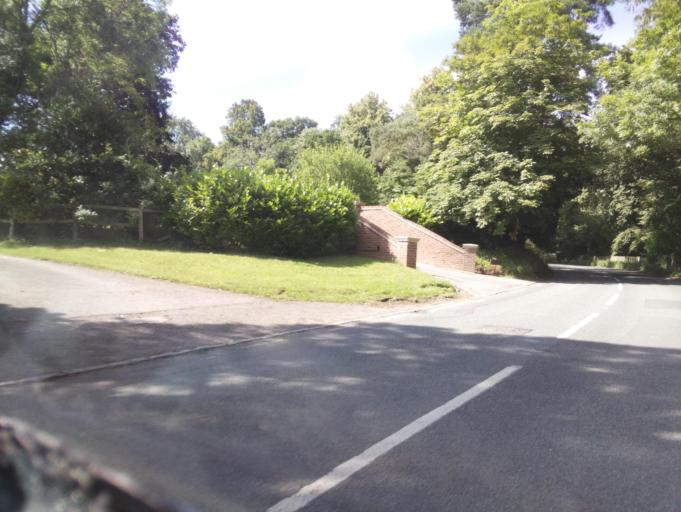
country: GB
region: England
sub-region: West Berkshire
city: Newbury
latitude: 51.4243
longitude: -1.3318
